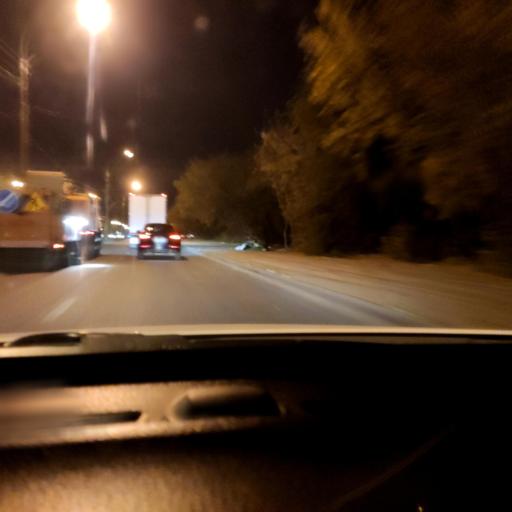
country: RU
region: Voronezj
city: Voronezh
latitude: 51.6362
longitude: 39.1707
